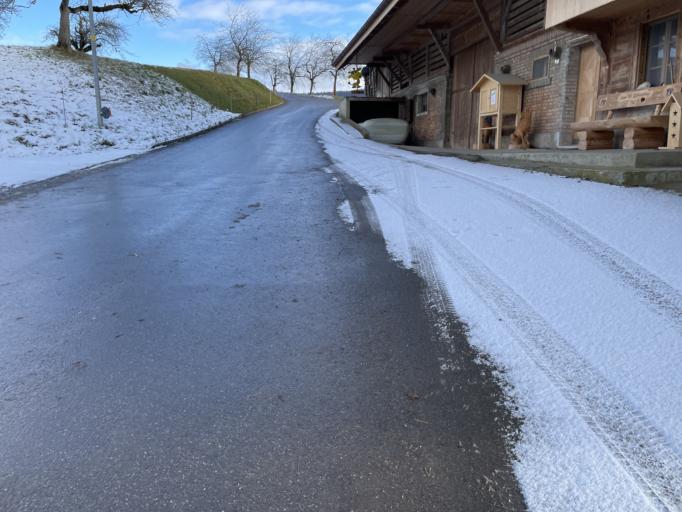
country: CH
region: Lucerne
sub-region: Entlebuch District
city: Oberdiessbach
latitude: 46.8574
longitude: 7.6069
